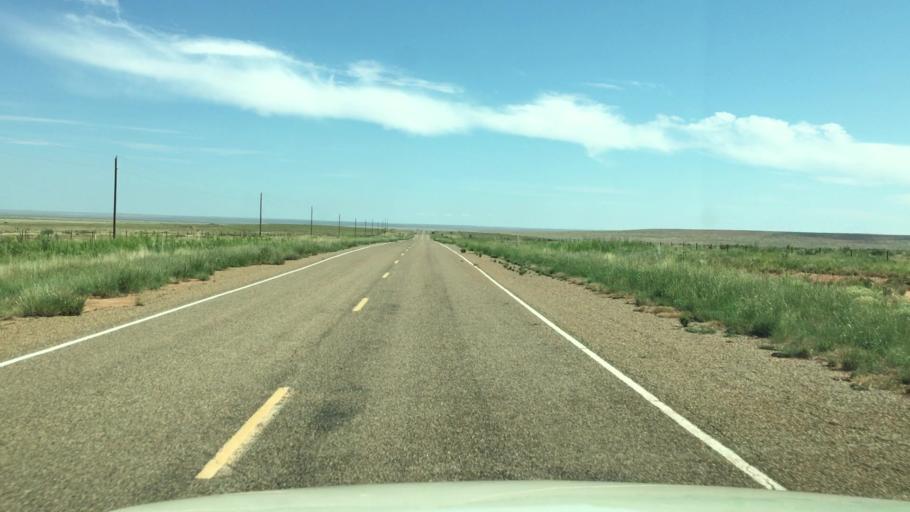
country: US
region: New Mexico
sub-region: De Baca County
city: Fort Sumner
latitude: 33.9939
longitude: -104.5690
